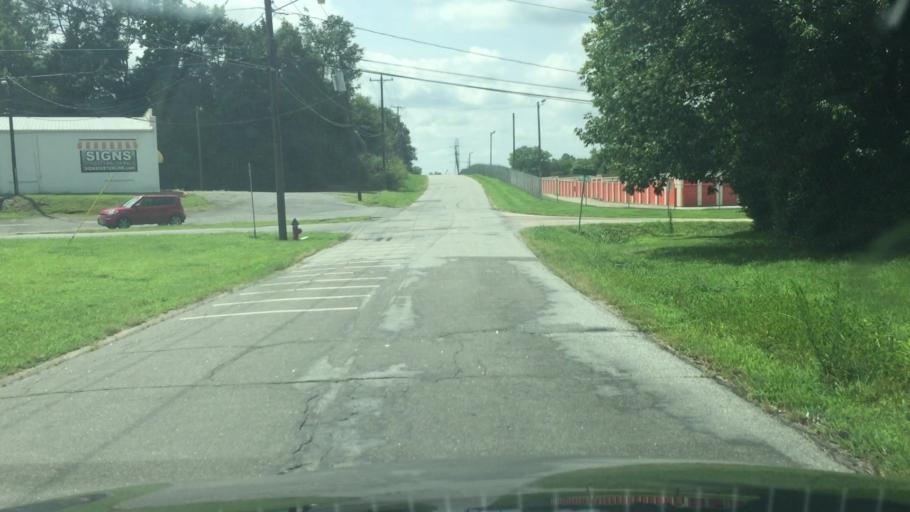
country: US
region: North Carolina
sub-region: Cabarrus County
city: Kannapolis
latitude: 35.4553
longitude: -80.6068
